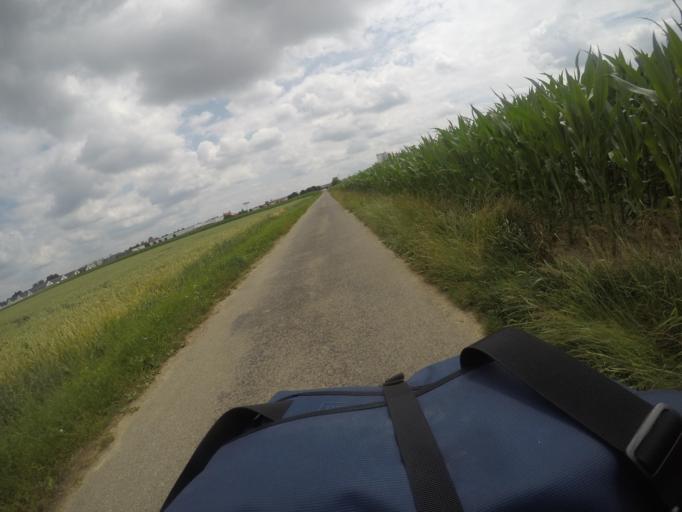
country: DE
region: Bavaria
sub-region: Swabia
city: Memmingen
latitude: 48.0073
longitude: 10.1660
